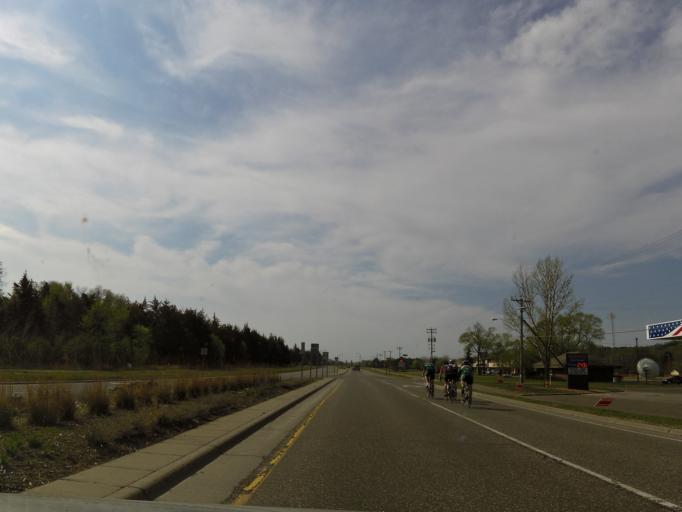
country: US
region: Minnesota
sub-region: Washington County
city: Lakeland
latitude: 44.9461
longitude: -92.7711
